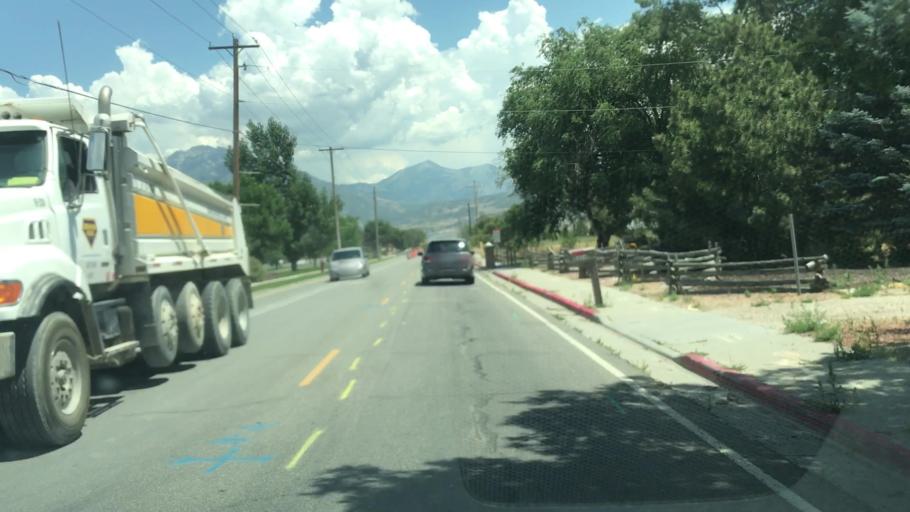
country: US
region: Utah
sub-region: Salt Lake County
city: Bluffdale
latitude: 40.4896
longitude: -111.9515
